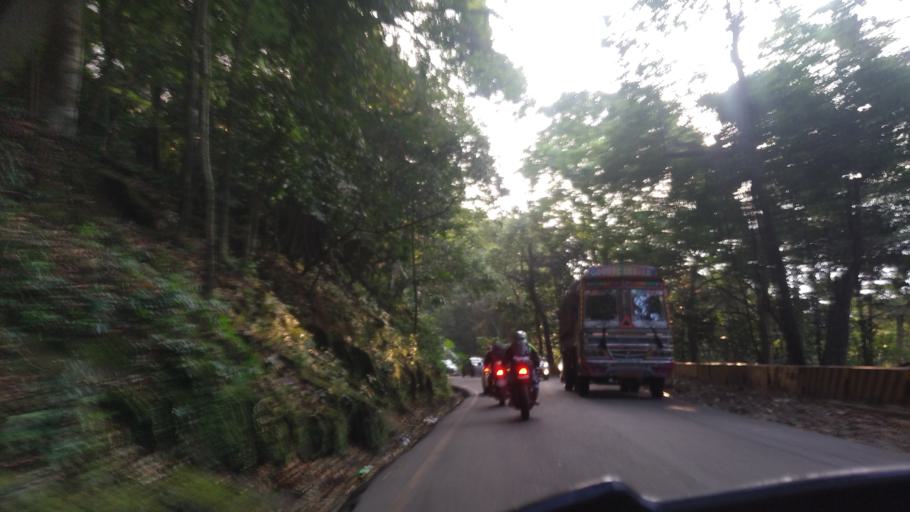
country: IN
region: Kerala
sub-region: Wayanad
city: Kalpetta
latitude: 11.5048
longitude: 76.0285
